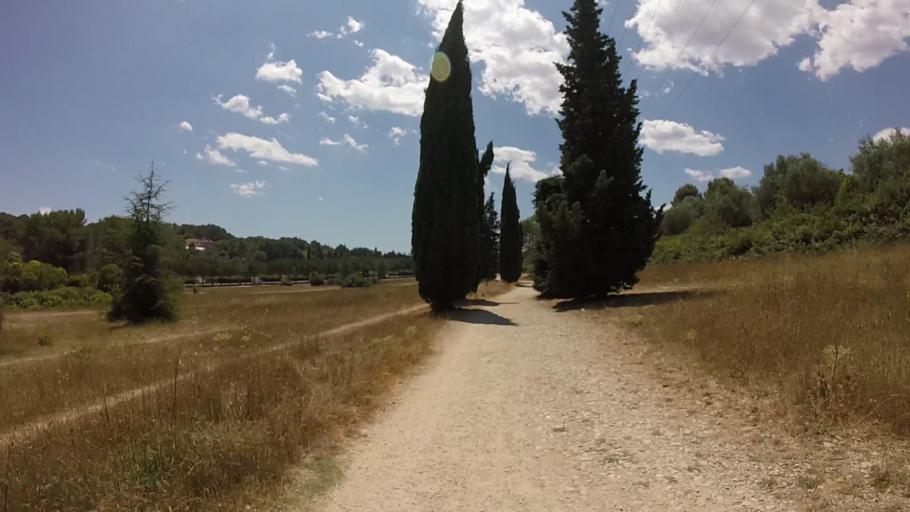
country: FR
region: Provence-Alpes-Cote d'Azur
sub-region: Departement des Alpes-Maritimes
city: Mougins
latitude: 43.5966
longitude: 7.0086
